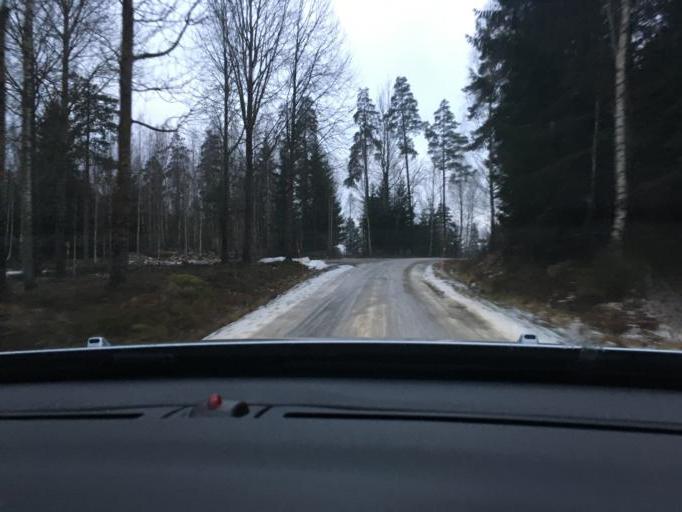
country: SE
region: Soedermanland
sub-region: Katrineholms Kommun
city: Katrineholm
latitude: 58.9829
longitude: 16.3185
